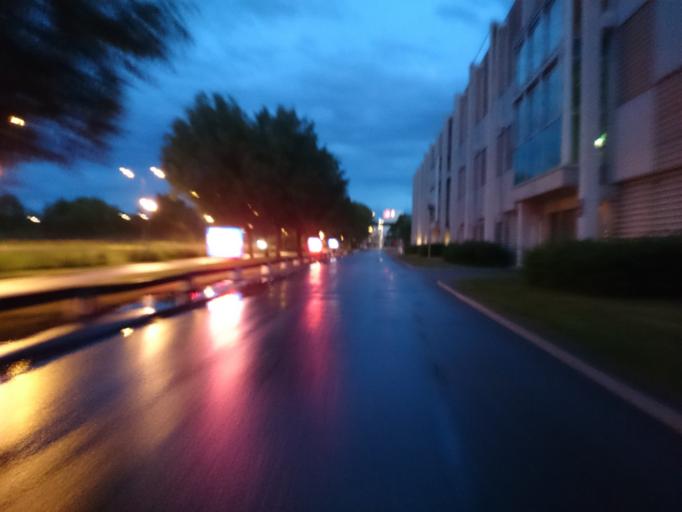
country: SE
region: Stockholm
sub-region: Stockholms Kommun
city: Arsta
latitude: 59.2773
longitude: 18.0181
